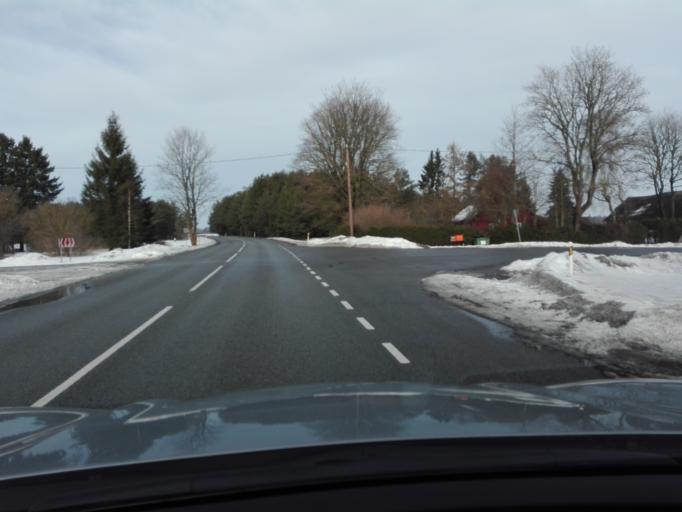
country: EE
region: Raplamaa
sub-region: Kehtna vald
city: Kehtna
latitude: 58.9005
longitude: 24.7875
